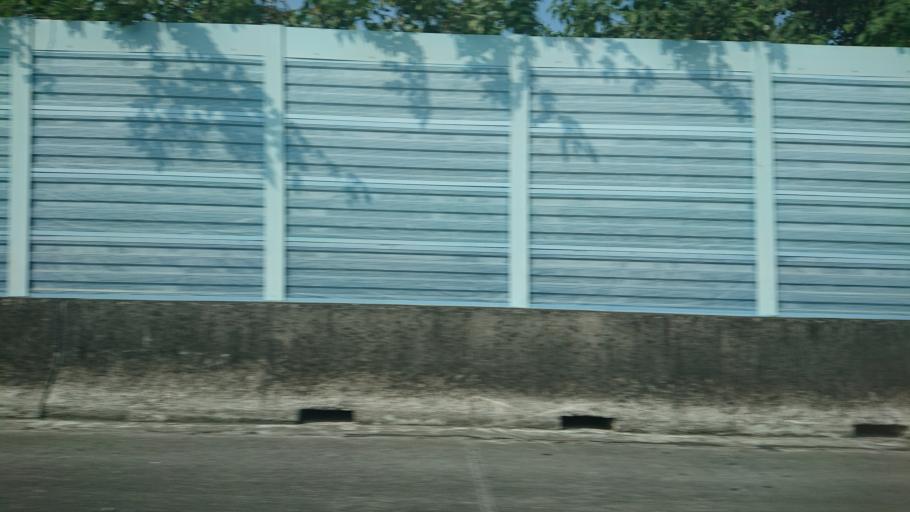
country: TW
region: Taiwan
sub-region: Nantou
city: Nantou
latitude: 23.8919
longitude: 120.7107
